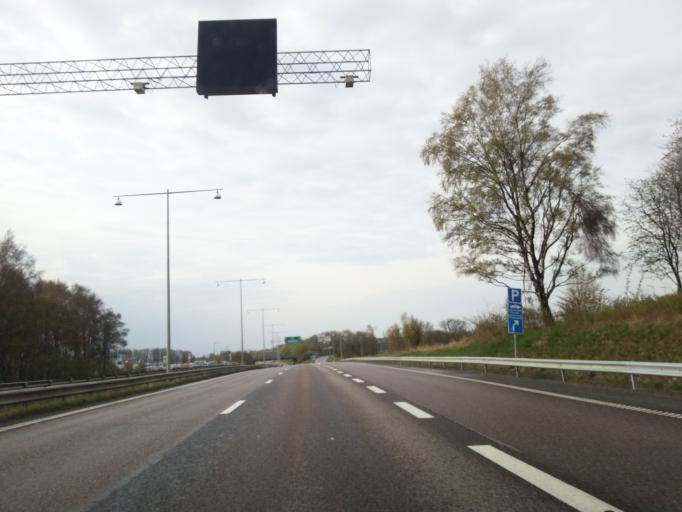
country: SE
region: Vaestra Goetaland
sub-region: Goteborg
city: Hammarkullen
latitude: 57.7623
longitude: 11.9928
